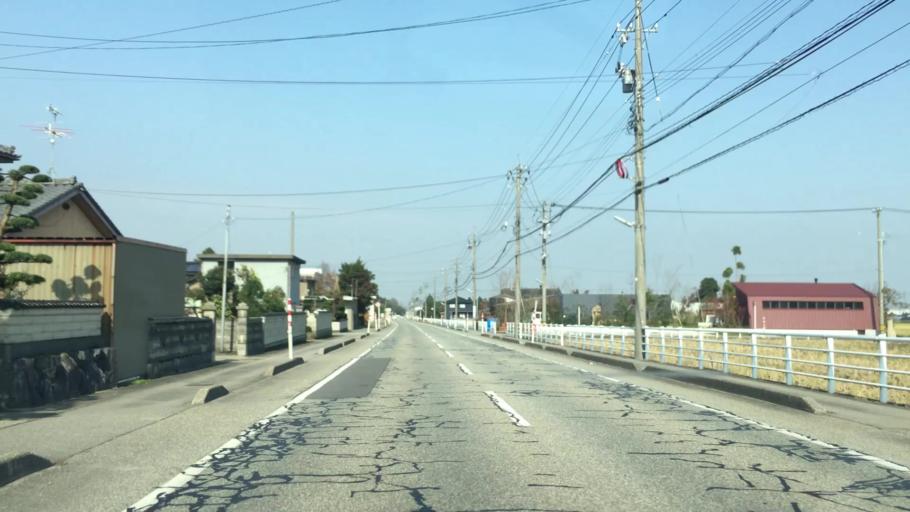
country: JP
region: Toyama
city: Yatsuomachi-higashikumisaka
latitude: 36.5826
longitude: 137.1922
